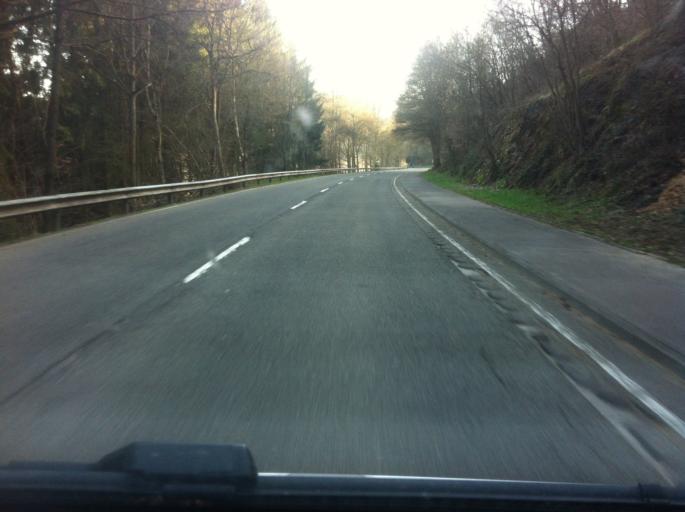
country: DE
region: North Rhine-Westphalia
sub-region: Regierungsbezirk Koln
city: Simmerath
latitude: 50.6106
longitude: 6.3750
